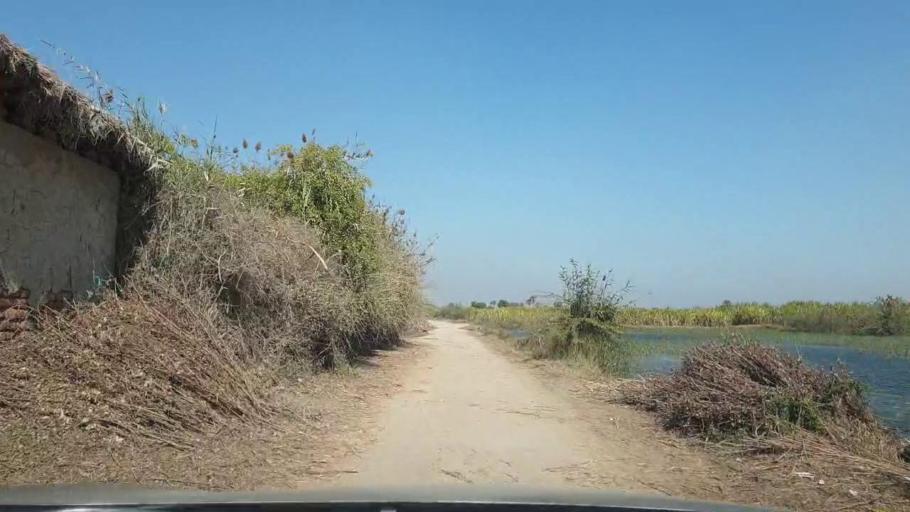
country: PK
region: Sindh
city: Tando Adam
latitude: 25.6324
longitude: 68.6672
